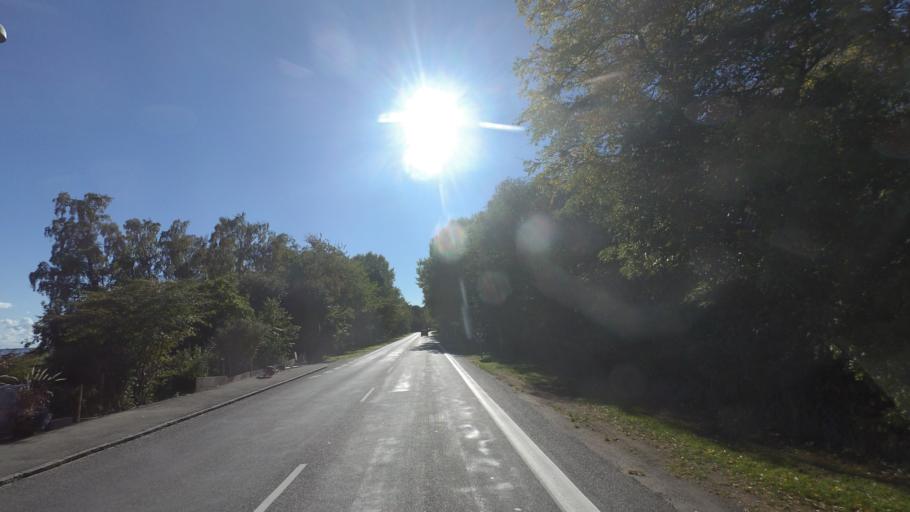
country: DK
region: Capital Region
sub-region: Bornholm Kommune
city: Nexo
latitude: 55.0538
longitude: 15.1238
